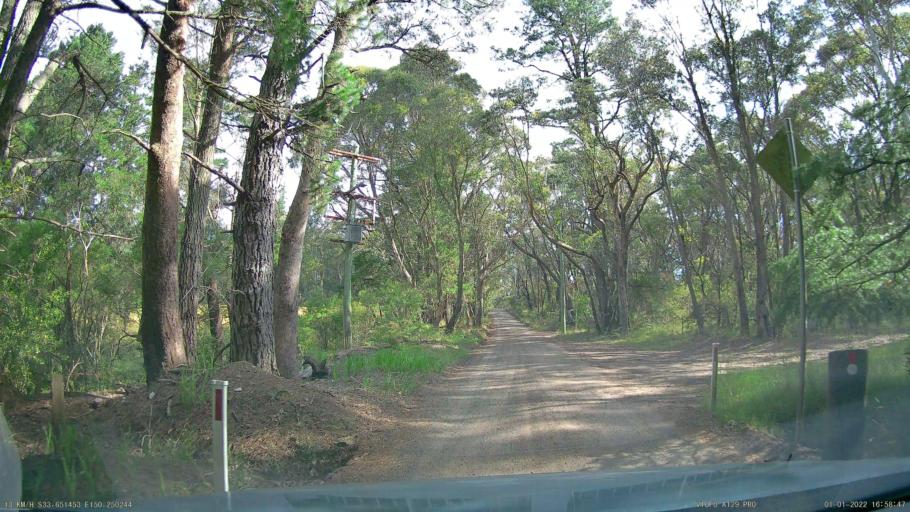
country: AU
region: New South Wales
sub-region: Blue Mountains Municipality
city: Blackheath
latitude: -33.6515
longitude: 150.2502
